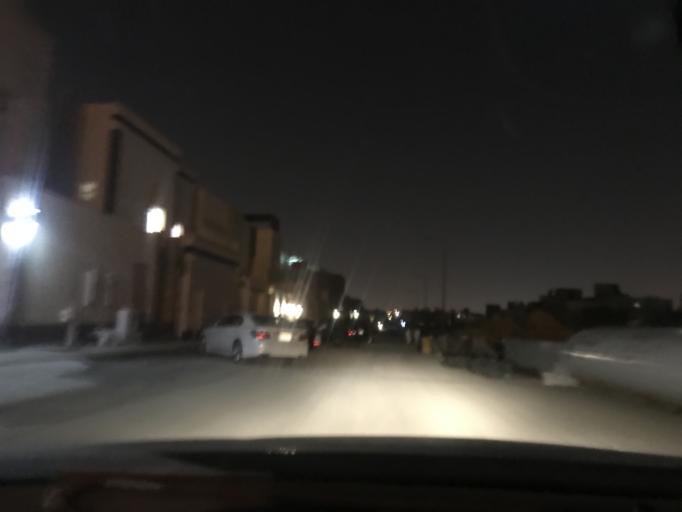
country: SA
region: Ar Riyad
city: Riyadh
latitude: 24.7473
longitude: 46.7544
